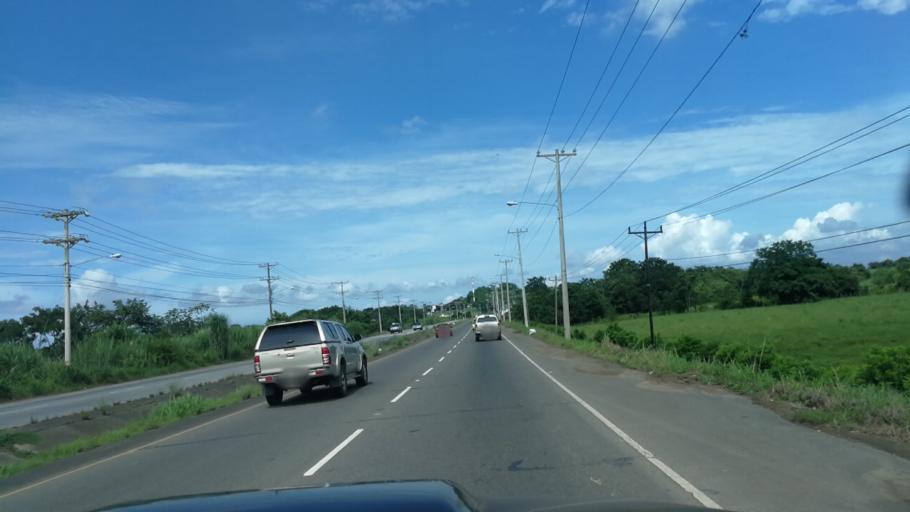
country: PA
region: Panama
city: Pacora
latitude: 9.1008
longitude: -79.2797
